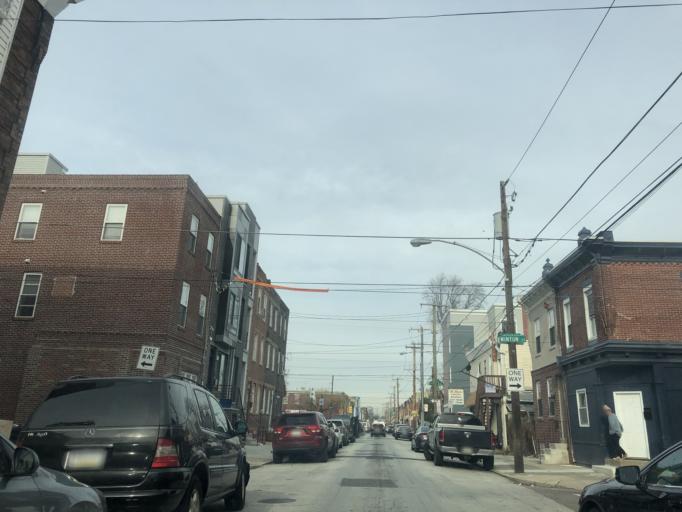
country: US
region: Pennsylvania
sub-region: Philadelphia County
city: Philadelphia
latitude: 39.9215
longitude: -75.1552
